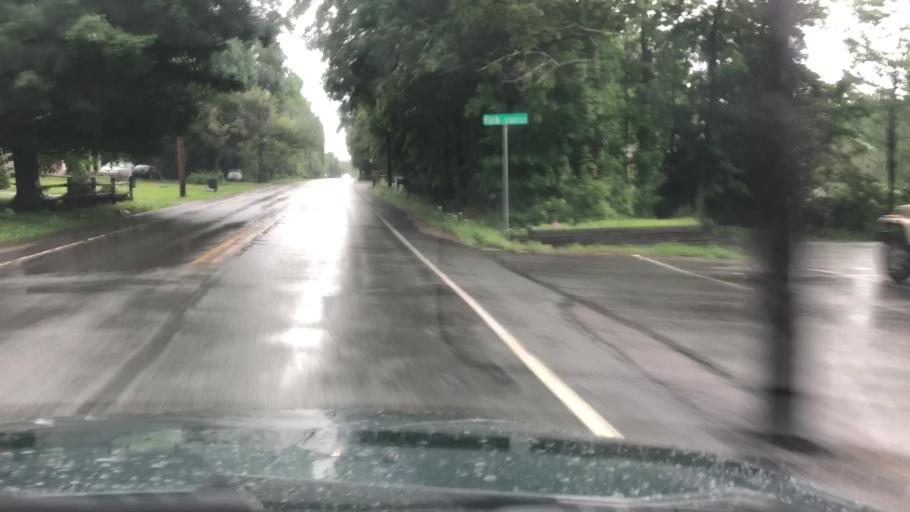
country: US
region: Pennsylvania
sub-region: Monroe County
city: Mountainhome
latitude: 41.1733
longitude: -75.2709
